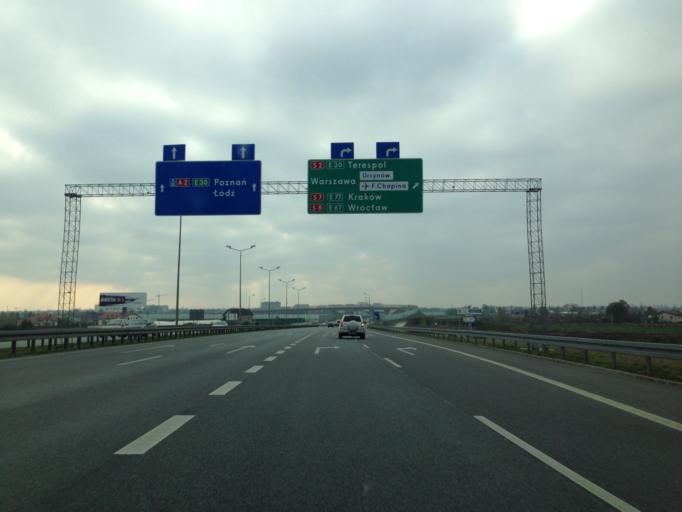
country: PL
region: Masovian Voivodeship
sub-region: Powiat pruszkowski
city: Piastow
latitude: 52.2064
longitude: 20.8515
